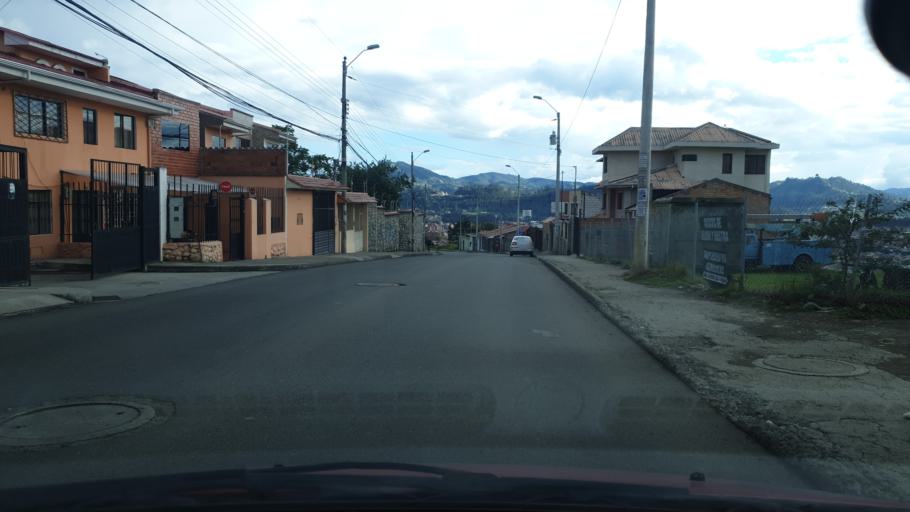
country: EC
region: Azuay
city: Cuenca
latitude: -2.8860
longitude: -79.0152
